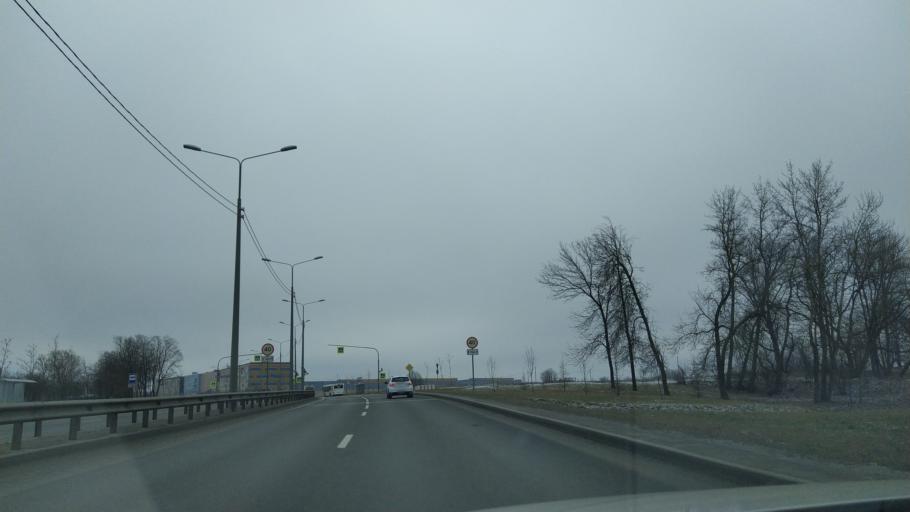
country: RU
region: St.-Petersburg
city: Aleksandrovskaya
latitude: 59.7698
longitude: 30.3447
